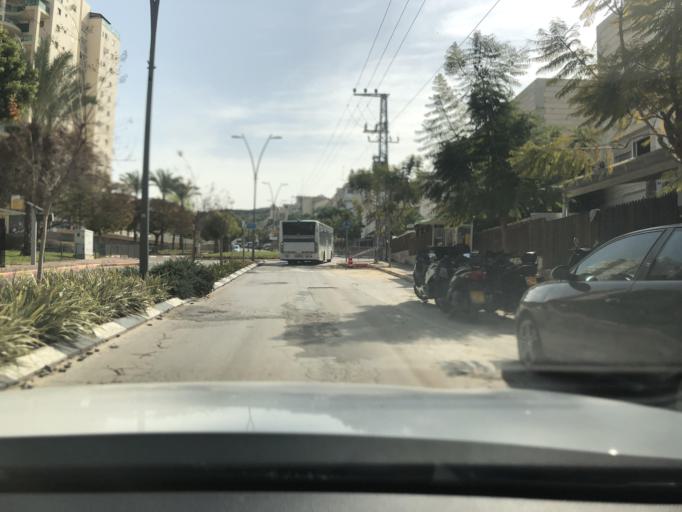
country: IL
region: Central District
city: Rosh Ha'Ayin
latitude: 32.0870
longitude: 34.9553
